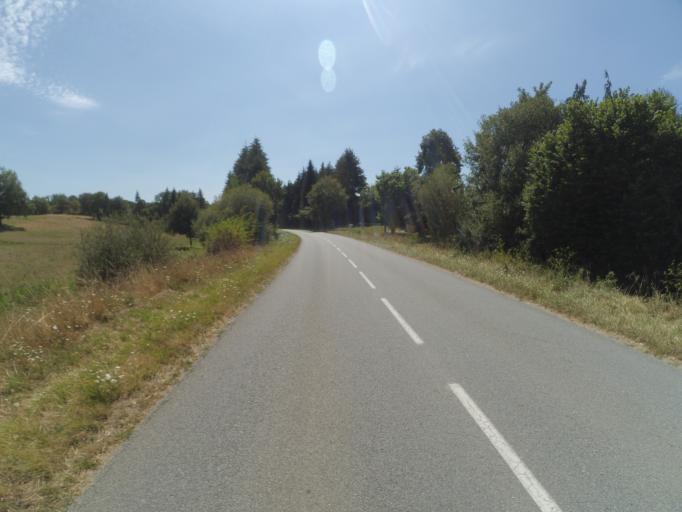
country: FR
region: Limousin
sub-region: Departement de la Creuse
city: Le Grand-Bourg
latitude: 46.0990
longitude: 1.6771
